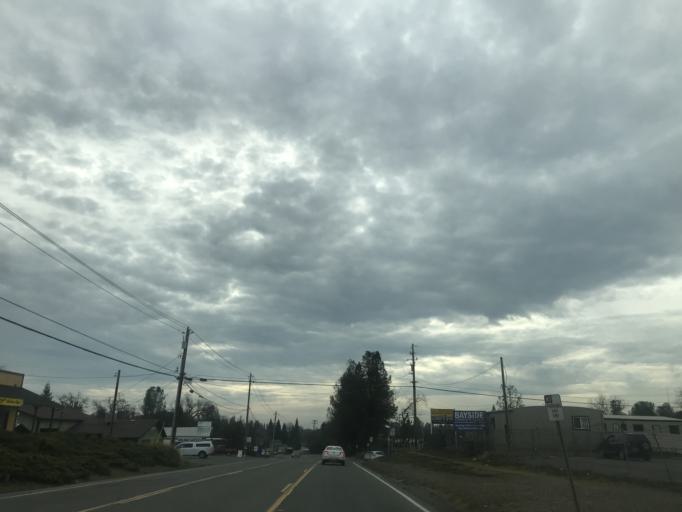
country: US
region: California
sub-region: El Dorado County
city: Diamond Springs
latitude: 38.6971
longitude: -120.8235
